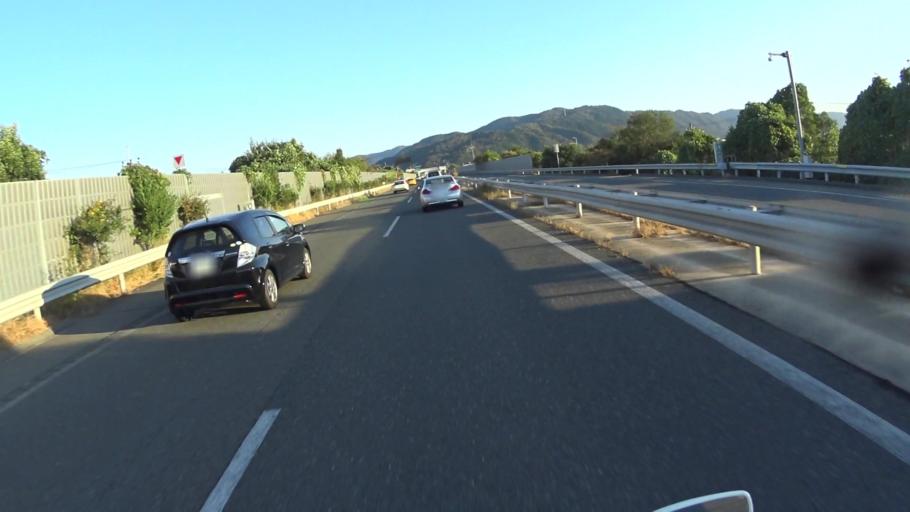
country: JP
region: Kyoto
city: Kameoka
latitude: 35.0199
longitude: 135.5524
